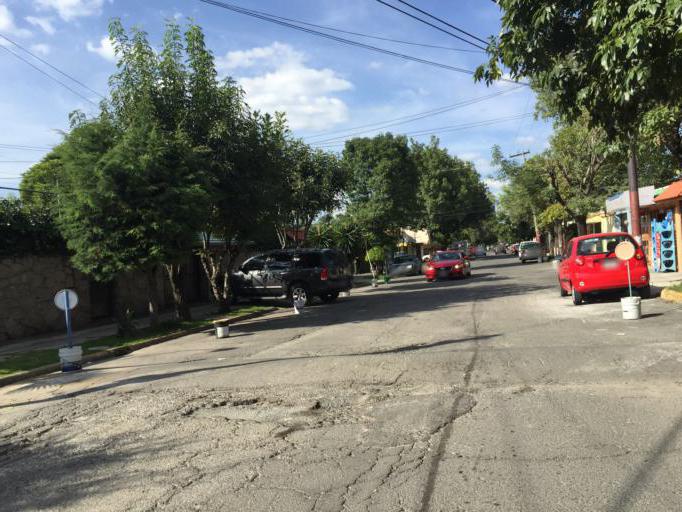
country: MX
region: Mexico
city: Cuautitlan Izcalli
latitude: 19.6648
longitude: -99.2073
